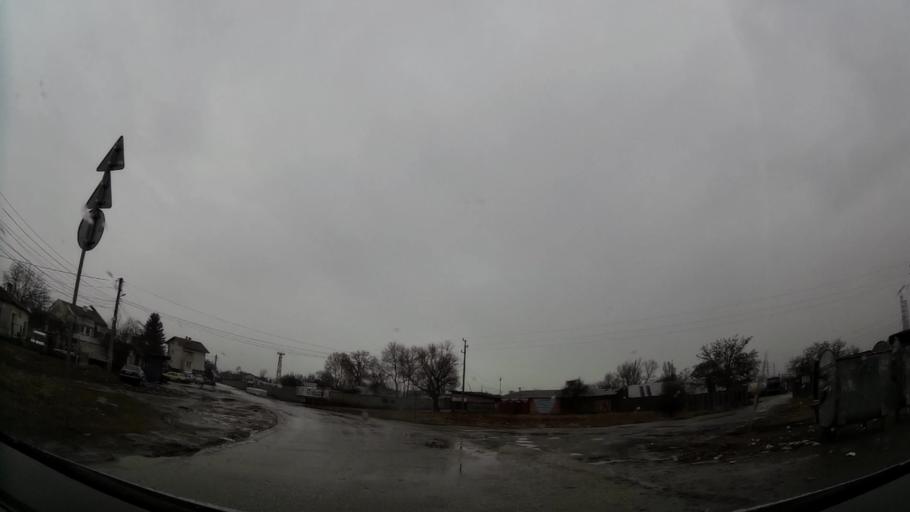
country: BG
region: Sofia-Capital
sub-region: Stolichna Obshtina
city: Sofia
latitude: 42.6582
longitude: 23.4253
